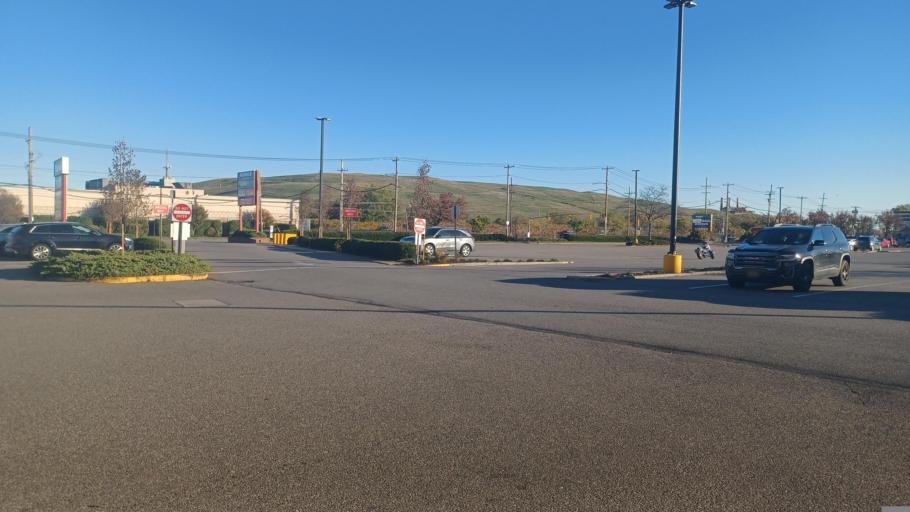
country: US
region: New York
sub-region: Nassau County
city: Oceanside
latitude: 40.6232
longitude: -73.6411
